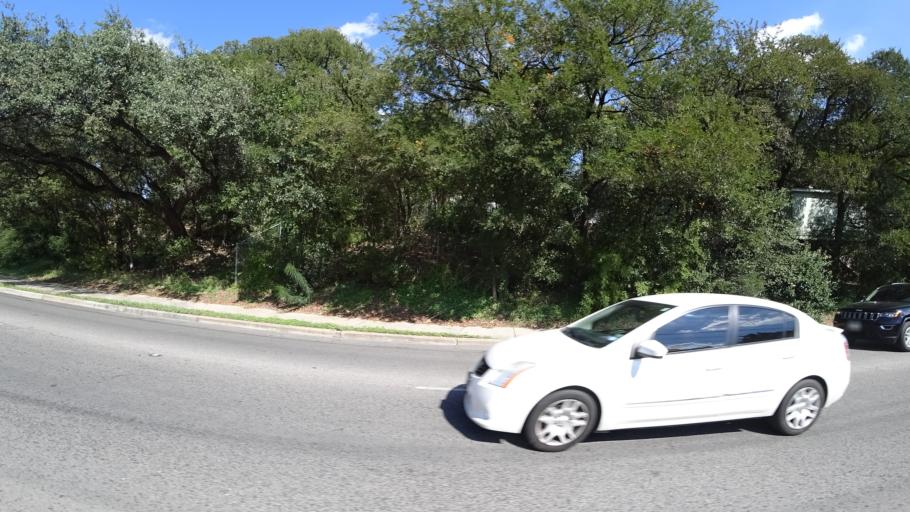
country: US
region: Texas
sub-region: Travis County
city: Austin
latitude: 30.2962
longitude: -97.7489
